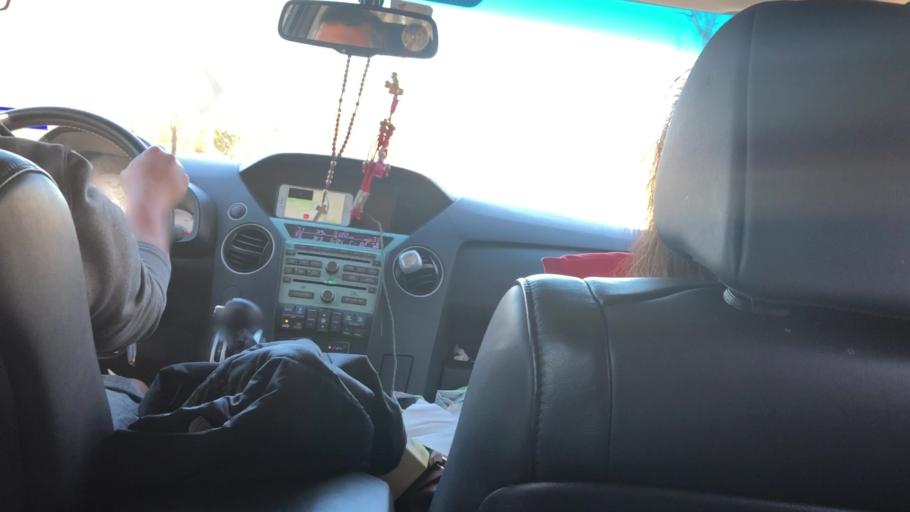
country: US
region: Louisiana
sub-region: Saint John the Baptist Parish
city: Montegut
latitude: 30.1044
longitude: -90.4925
